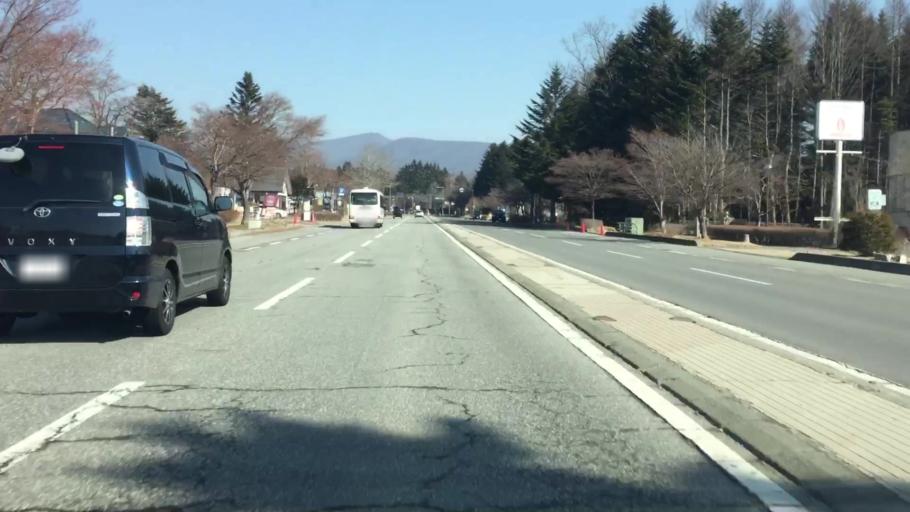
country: JP
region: Nagano
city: Saku
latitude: 36.3303
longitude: 138.6305
